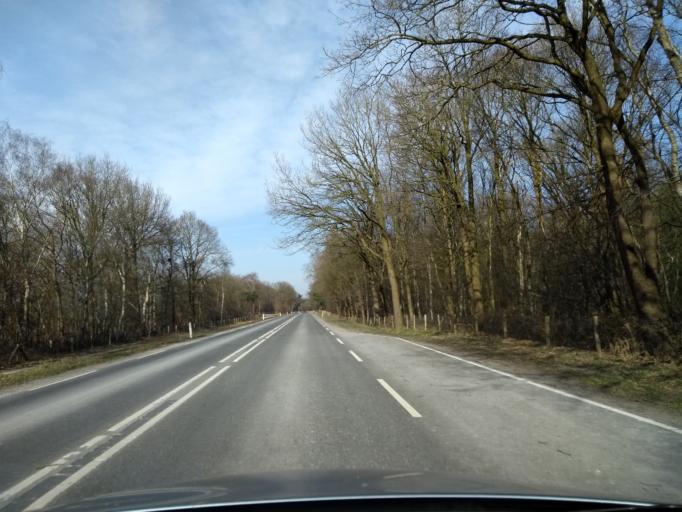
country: DE
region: Lower Saxony
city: Wielen
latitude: 52.4810
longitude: 6.6959
